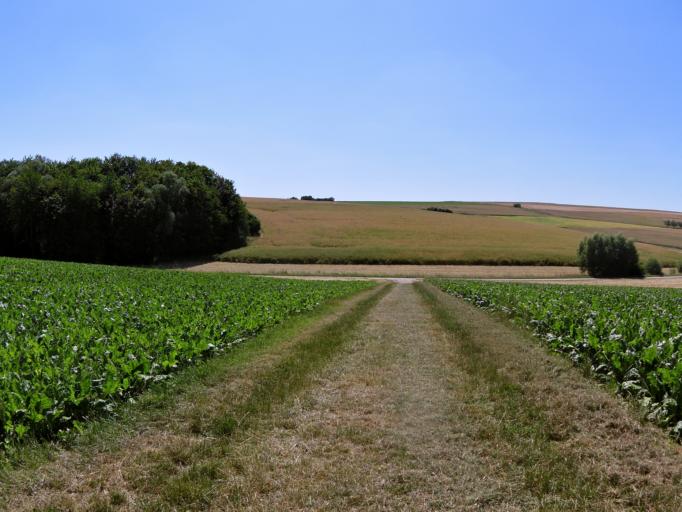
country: DE
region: Bavaria
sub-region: Regierungsbezirk Unterfranken
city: Reichenberg
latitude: 49.7221
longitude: 9.9020
